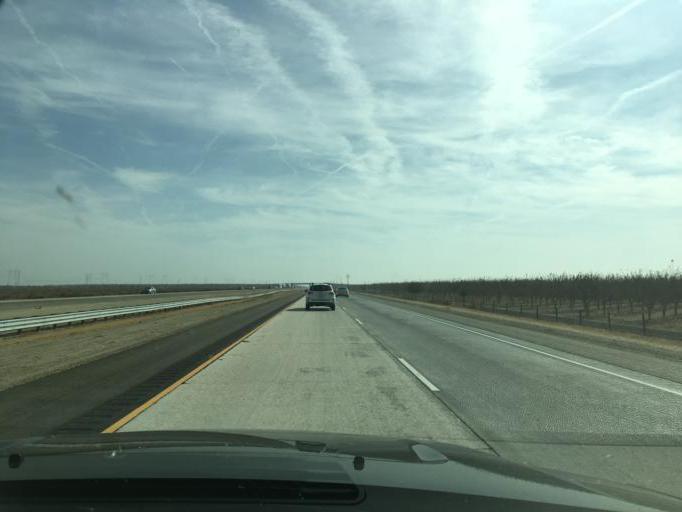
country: US
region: California
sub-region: Kern County
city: Lost Hills
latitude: 35.5347
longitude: -119.5728
